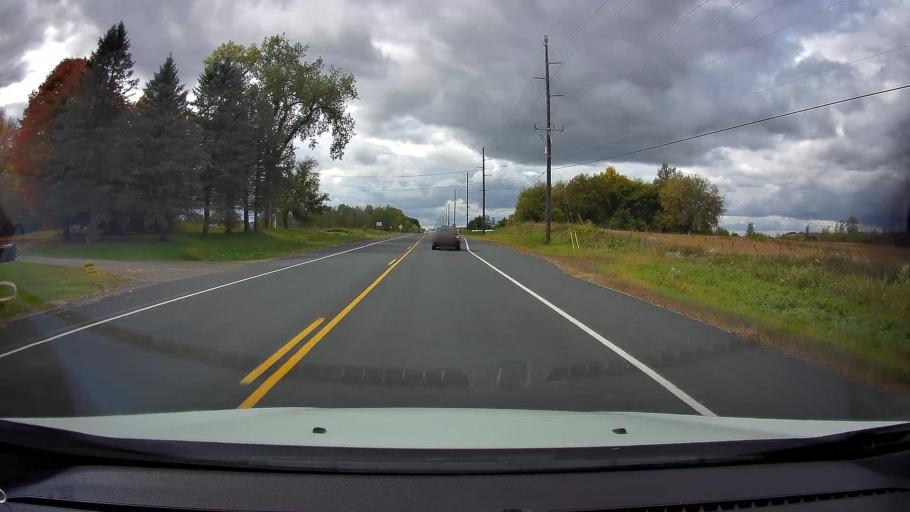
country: US
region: Minnesota
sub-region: Chisago County
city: Shafer
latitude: 45.3974
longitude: -92.7413
